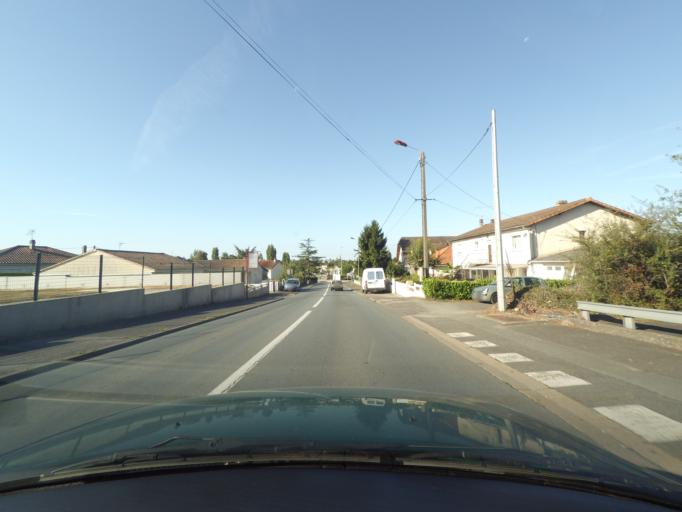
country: FR
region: Poitou-Charentes
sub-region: Departement des Deux-Sevres
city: Chatillon-sur-Thouet
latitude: 46.6640
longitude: -0.2377
